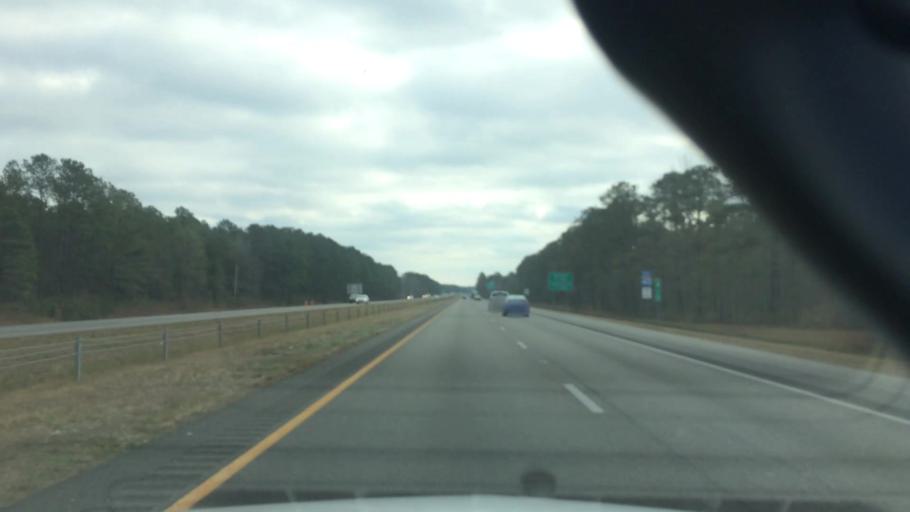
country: US
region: North Carolina
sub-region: New Hanover County
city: Skippers Corner
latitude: 34.3448
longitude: -77.8813
